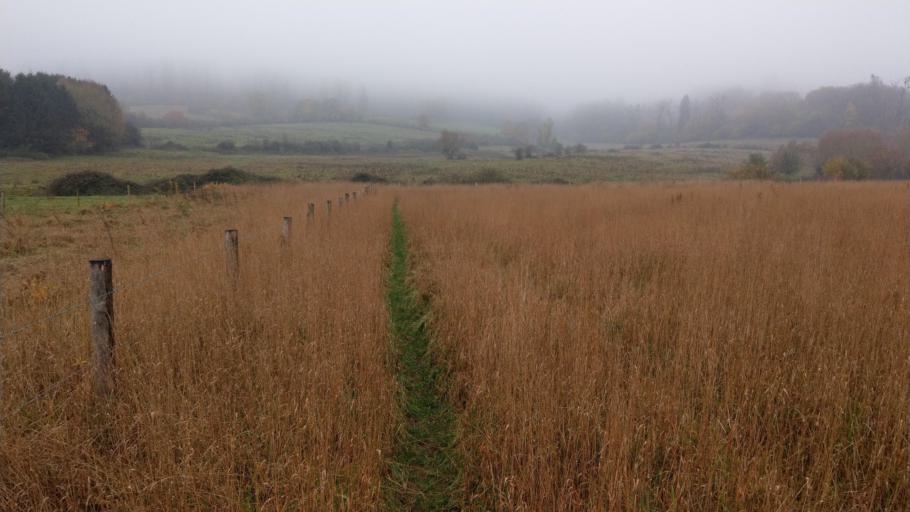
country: NL
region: Limburg
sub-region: Gemeente Vaals
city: Vaals
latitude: 50.7621
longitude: 5.9939
